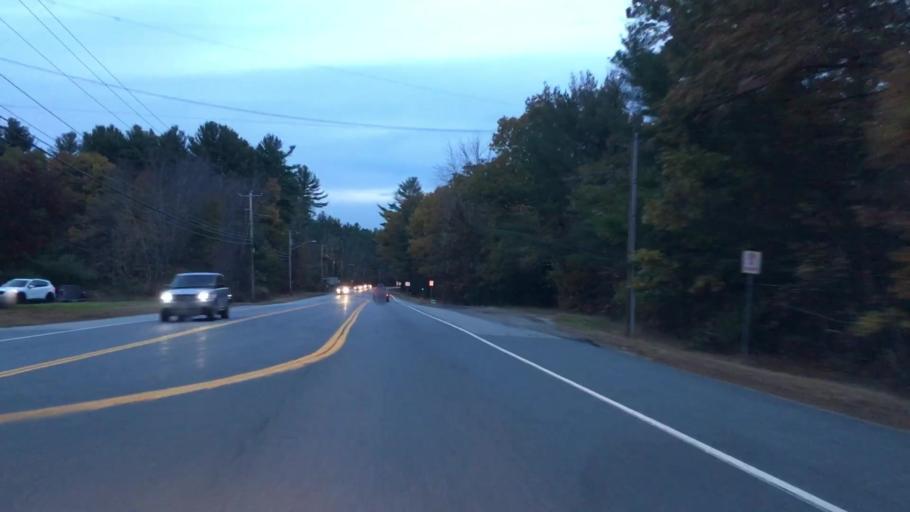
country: US
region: New Hampshire
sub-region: Hillsborough County
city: Milford
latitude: 42.8744
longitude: -71.6130
